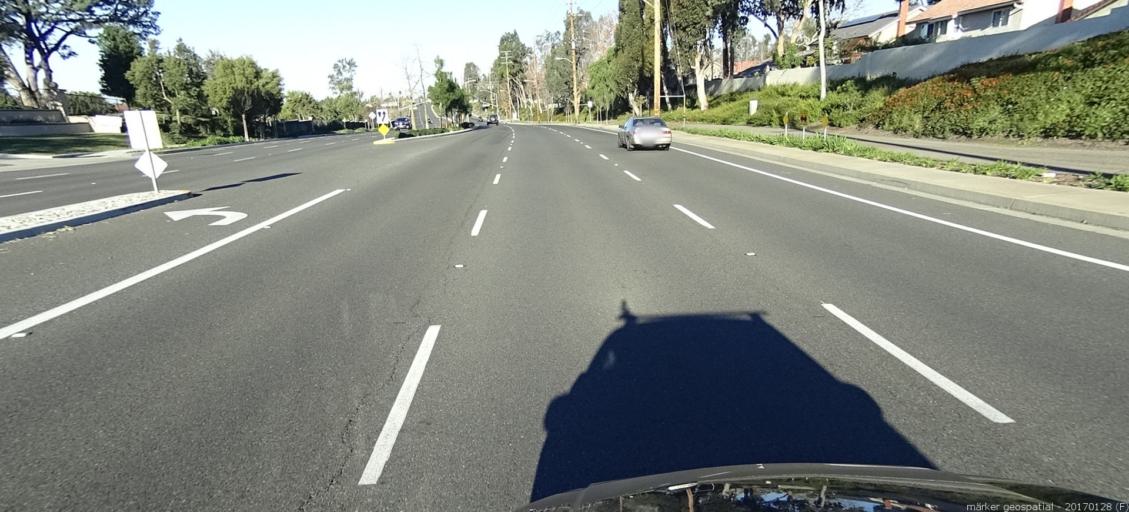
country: US
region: California
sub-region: Orange County
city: Lake Forest
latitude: 33.6515
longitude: -117.6930
